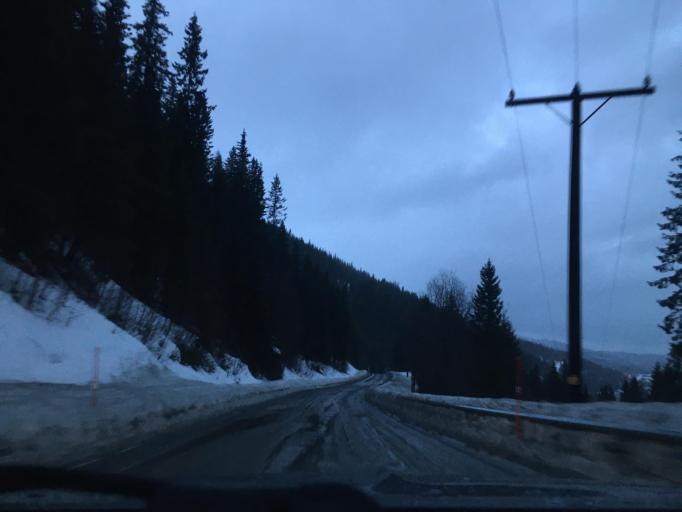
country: NO
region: Nordland
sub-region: Rana
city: Hauknes
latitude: 66.2852
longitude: 13.9068
